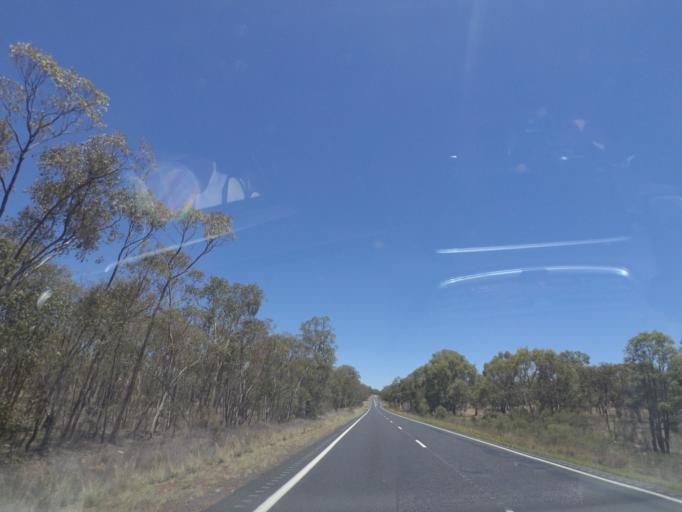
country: AU
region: New South Wales
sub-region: Warrumbungle Shire
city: Coonabarabran
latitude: -31.2228
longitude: 149.3239
